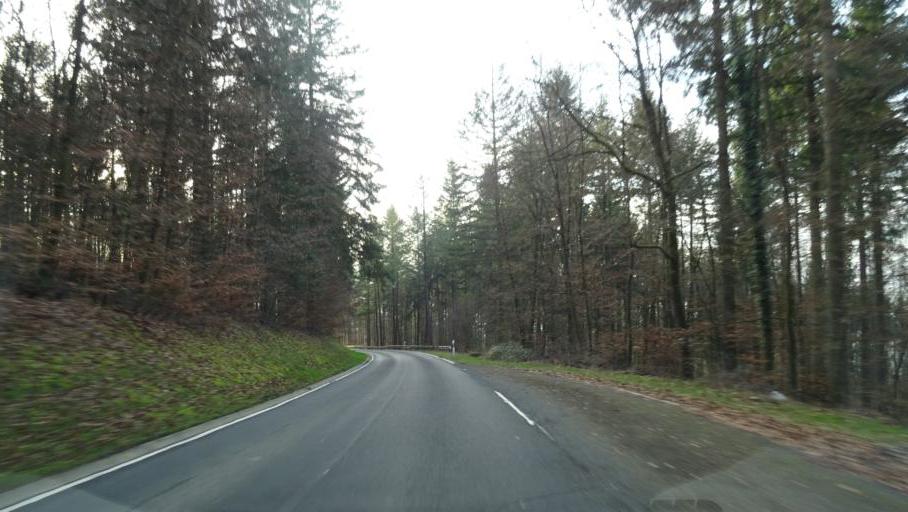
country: DE
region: Baden-Wuerttemberg
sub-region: Karlsruhe Region
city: Mosbach
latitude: 49.3396
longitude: 9.1368
